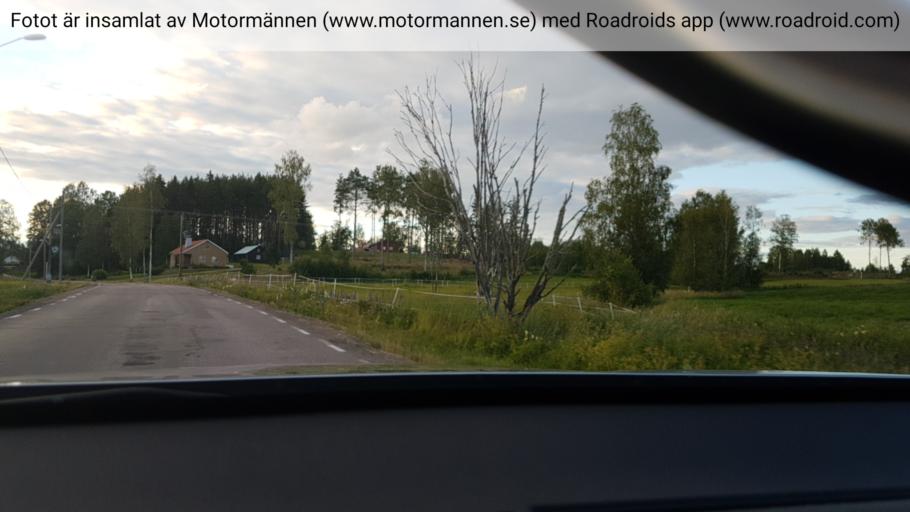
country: SE
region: Vaermland
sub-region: Torsby Kommun
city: Torsby
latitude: 60.1487
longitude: 13.0223
